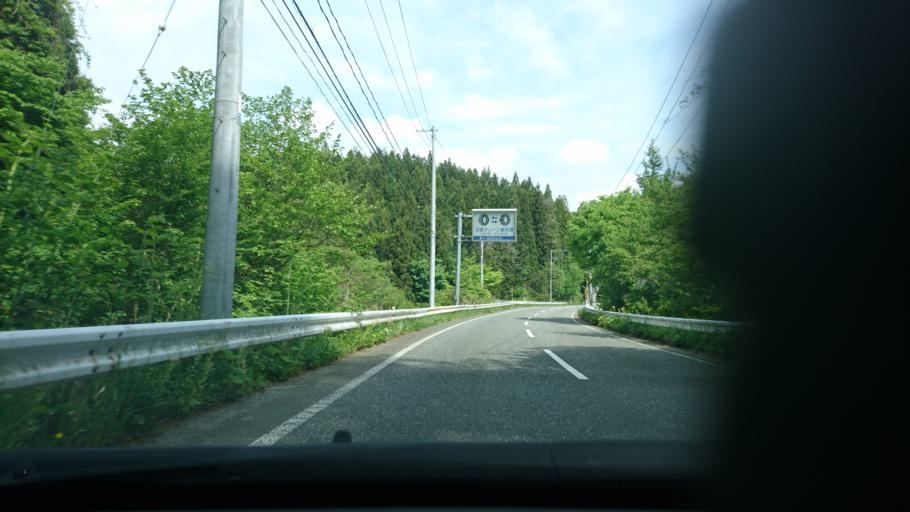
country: JP
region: Iwate
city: Ichinoseki
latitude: 38.8998
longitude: 140.9047
